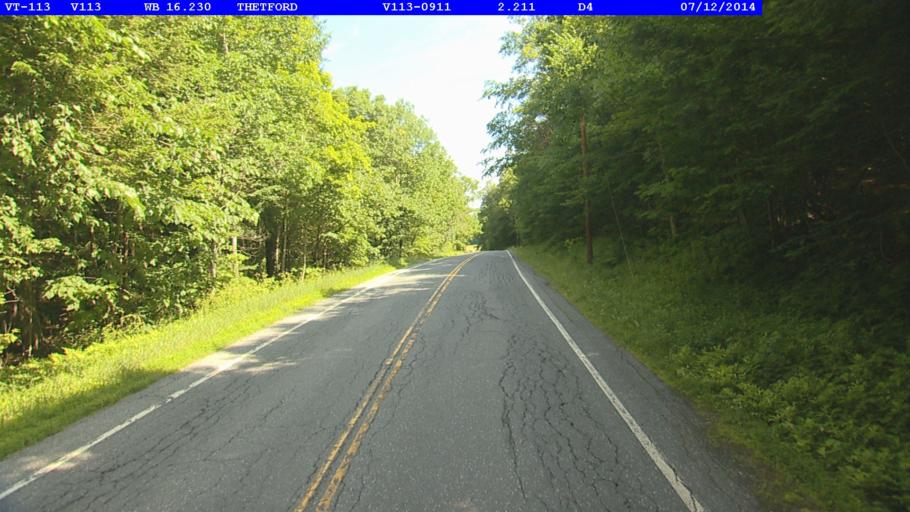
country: US
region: New Hampshire
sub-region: Grafton County
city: Lyme
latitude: 43.8669
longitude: -72.2610
